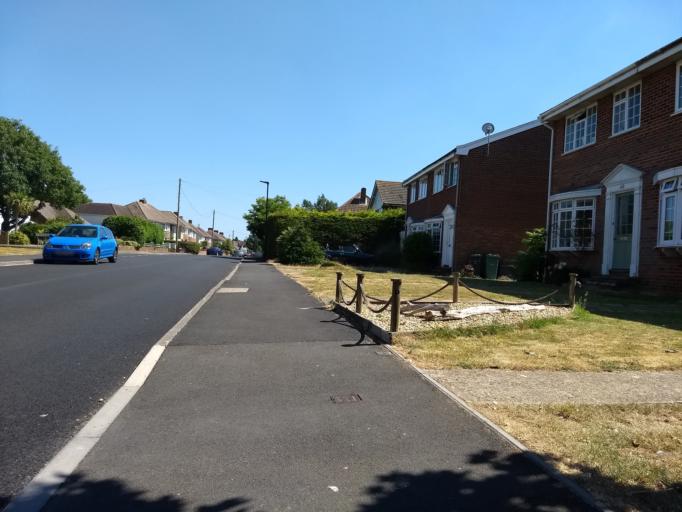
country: GB
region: England
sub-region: Isle of Wight
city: Gurnard
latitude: 50.7591
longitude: -1.3113
